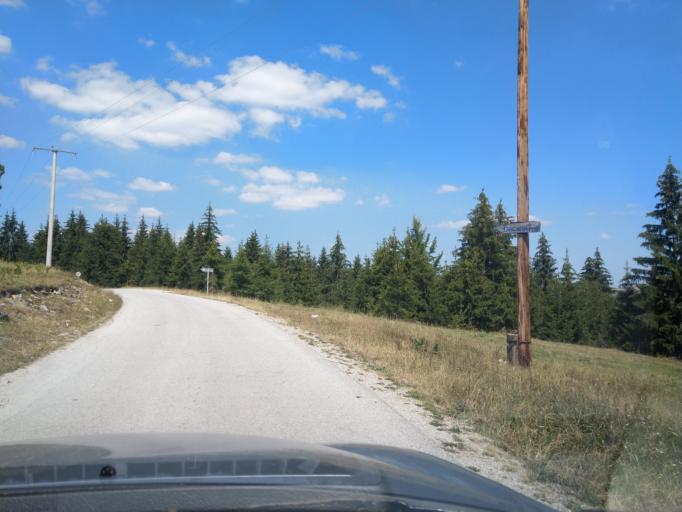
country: RS
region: Central Serbia
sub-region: Zlatiborski Okrug
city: Nova Varos
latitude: 43.4684
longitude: 19.9722
